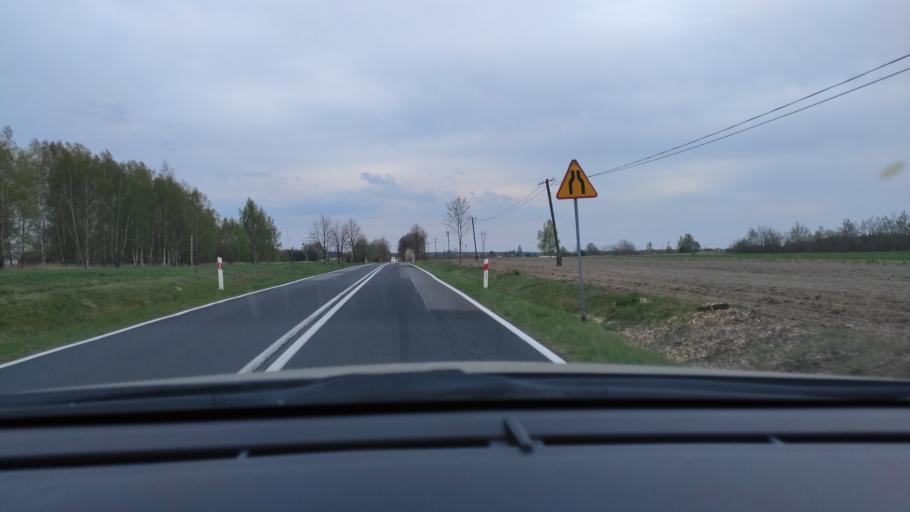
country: PL
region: Masovian Voivodeship
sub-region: Powiat zwolenski
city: Zwolen
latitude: 51.3716
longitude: 21.5635
